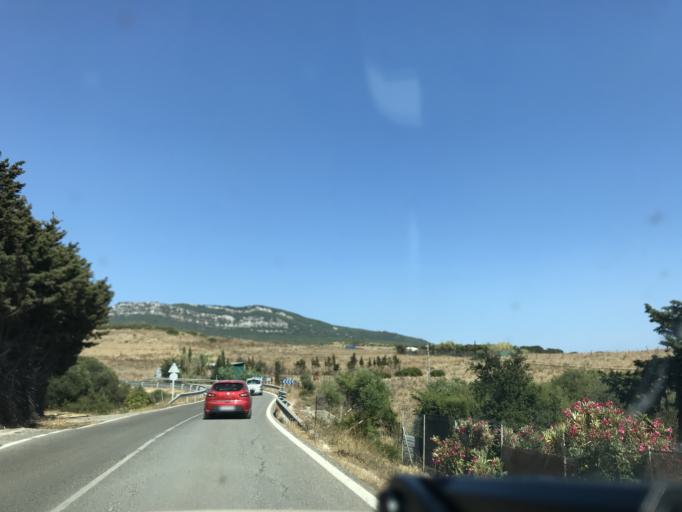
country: ES
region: Andalusia
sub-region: Provincia de Cadiz
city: Zahara de los Atunes
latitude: 36.0879
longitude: -5.7623
